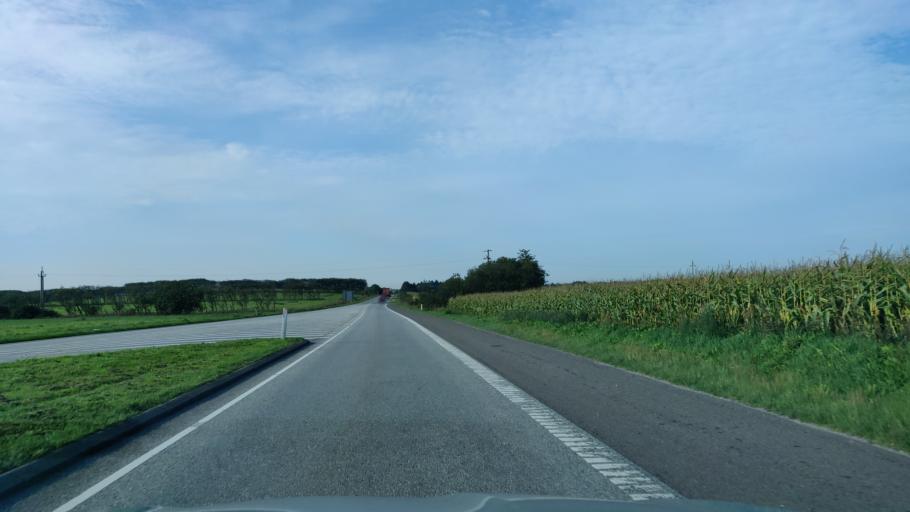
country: DK
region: North Denmark
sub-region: Vesthimmerland Kommune
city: Aars
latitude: 56.8081
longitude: 9.6514
